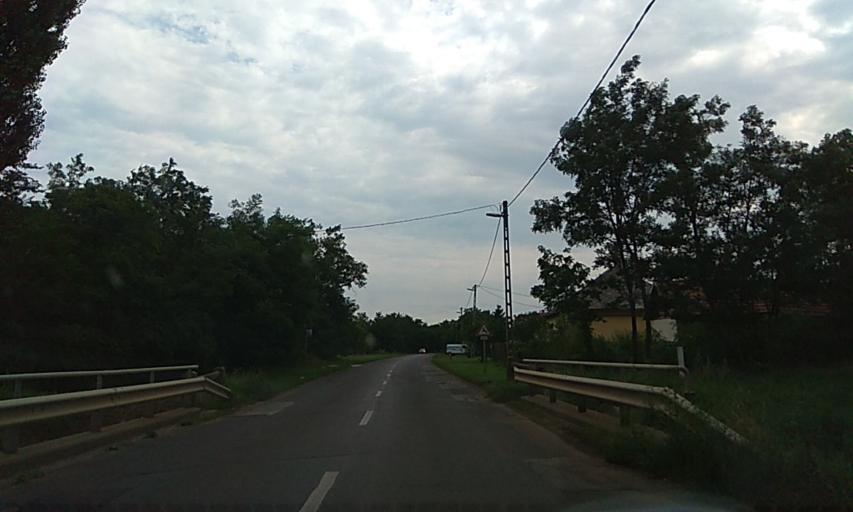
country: HU
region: Szabolcs-Szatmar-Bereg
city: Kotaj
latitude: 48.0270
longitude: 21.6776
